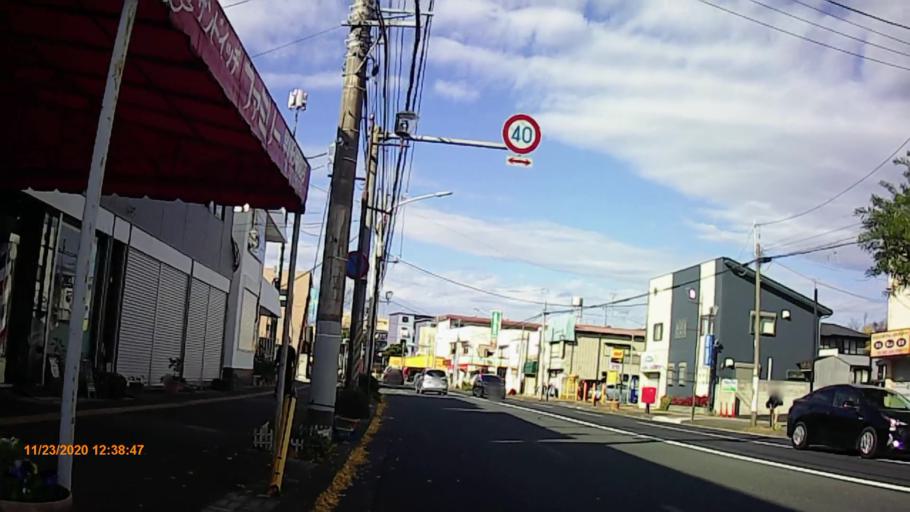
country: JP
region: Chiba
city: Yotsukaido
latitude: 35.6193
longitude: 140.1916
